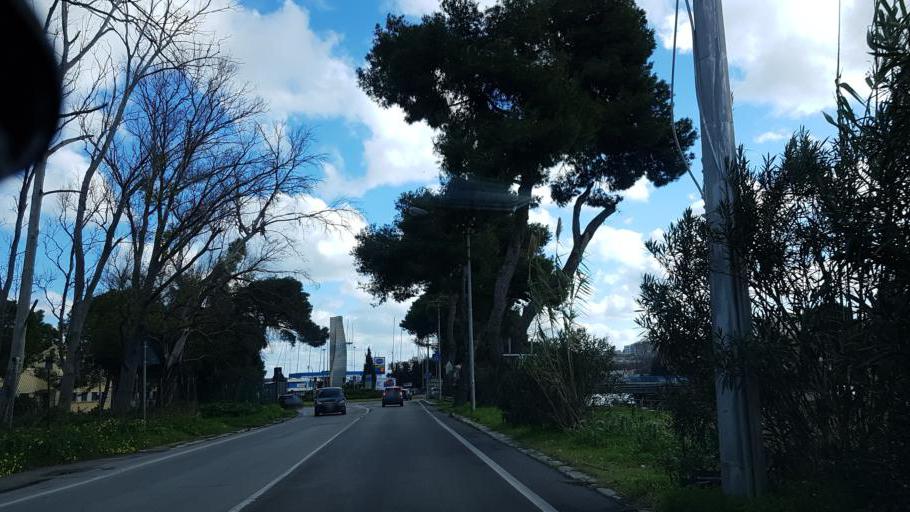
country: IT
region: Apulia
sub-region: Provincia di Brindisi
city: Brindisi
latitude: 40.6404
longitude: 17.9253
